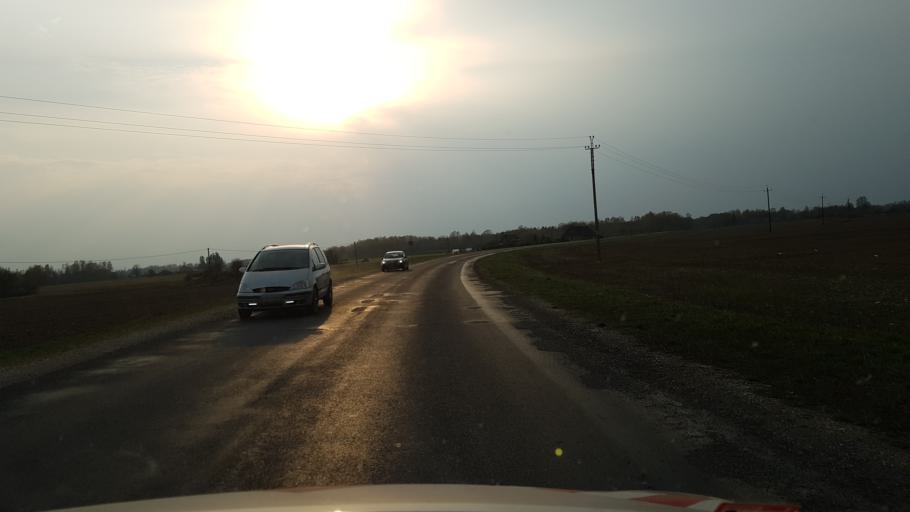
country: EE
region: Harju
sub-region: Raasiku vald
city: Raasiku
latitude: 59.3388
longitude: 25.1458
